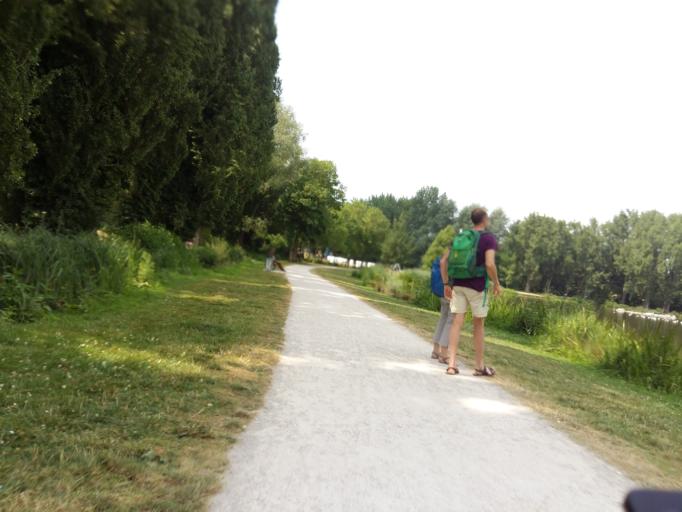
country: FR
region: Picardie
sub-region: Departement de la Somme
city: Amiens
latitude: 49.8983
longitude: 2.3097
